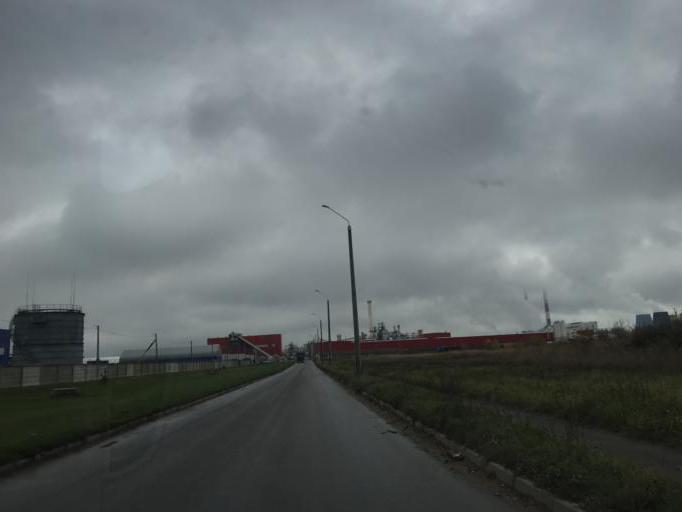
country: BY
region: Mogilev
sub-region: Mahilyowski Rayon
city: Veyno
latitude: 53.8266
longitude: 30.3525
